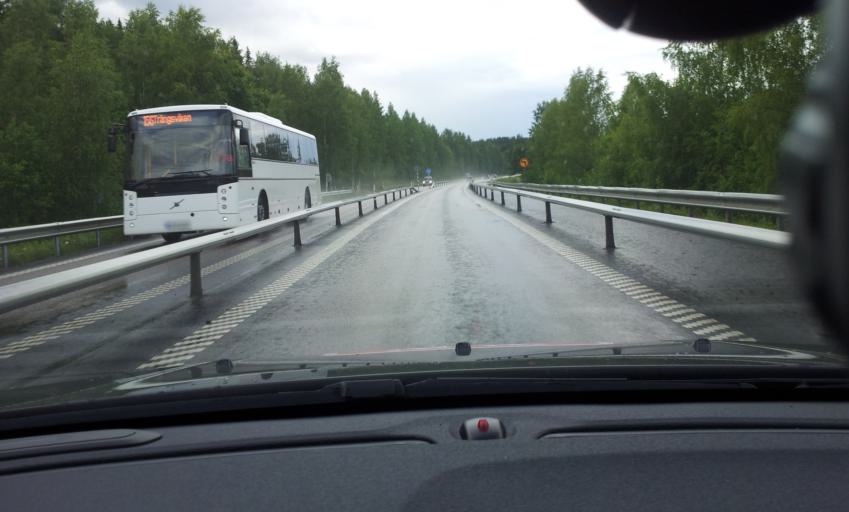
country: SE
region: Jaemtland
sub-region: Krokoms Kommun
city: Krokom
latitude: 63.3172
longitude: 14.4504
